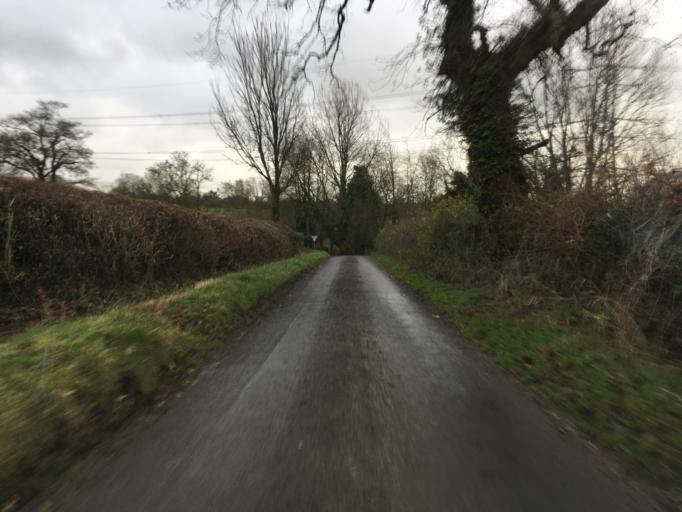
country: GB
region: England
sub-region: Wiltshire
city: Nettleton
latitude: 51.5088
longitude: -2.2689
